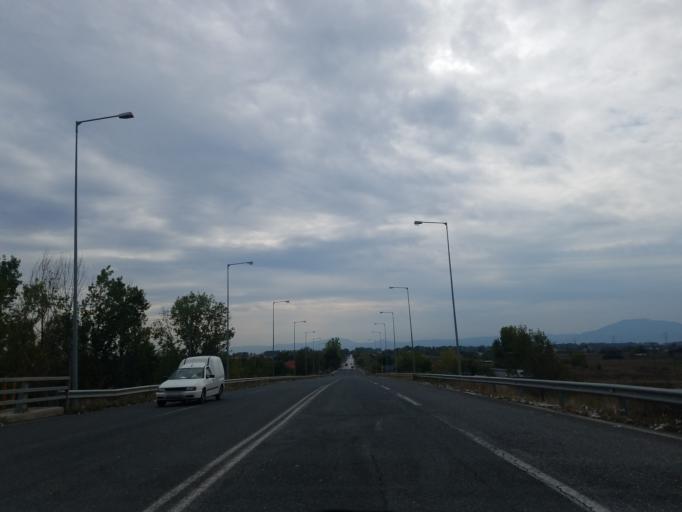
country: GR
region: Thessaly
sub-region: Nomos Kardhitsas
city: Sofades
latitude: 39.3410
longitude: 22.0820
